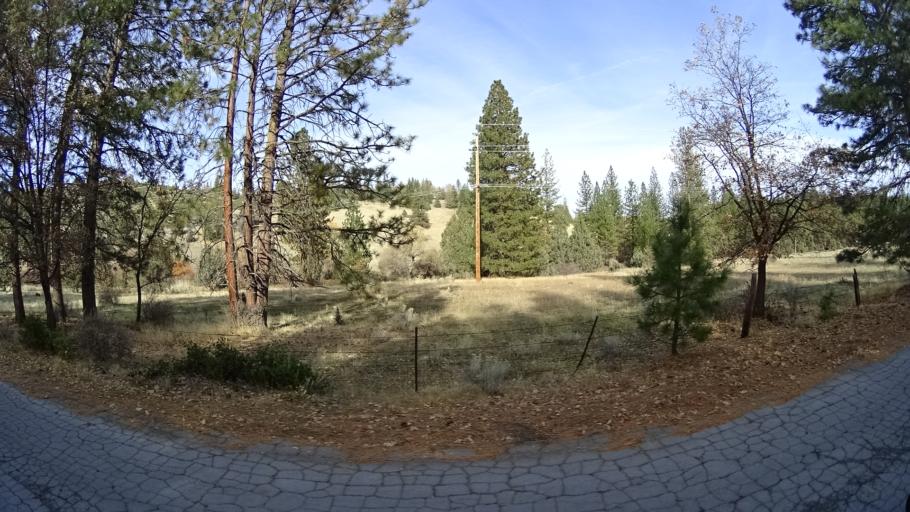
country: US
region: California
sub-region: Siskiyou County
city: Weed
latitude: 41.4668
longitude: -122.4071
